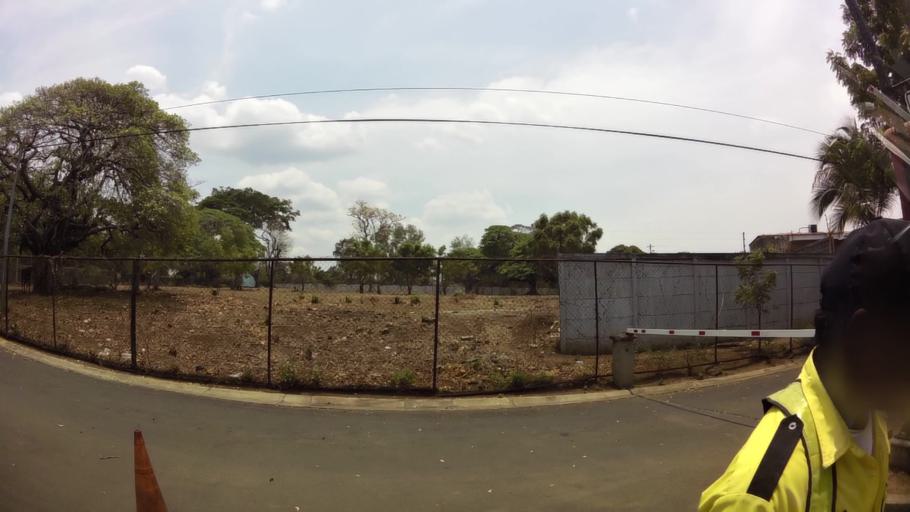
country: NI
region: Managua
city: Managua
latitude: 12.1151
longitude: -86.2868
